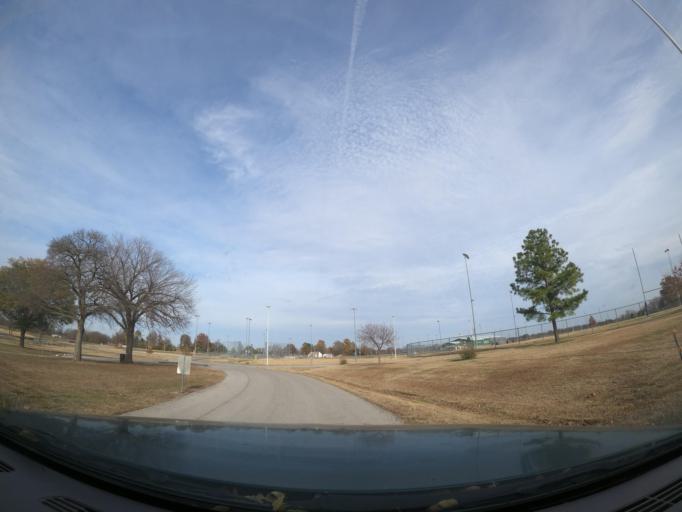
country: US
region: Oklahoma
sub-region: Tulsa County
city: Turley
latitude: 36.2468
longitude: -95.9539
